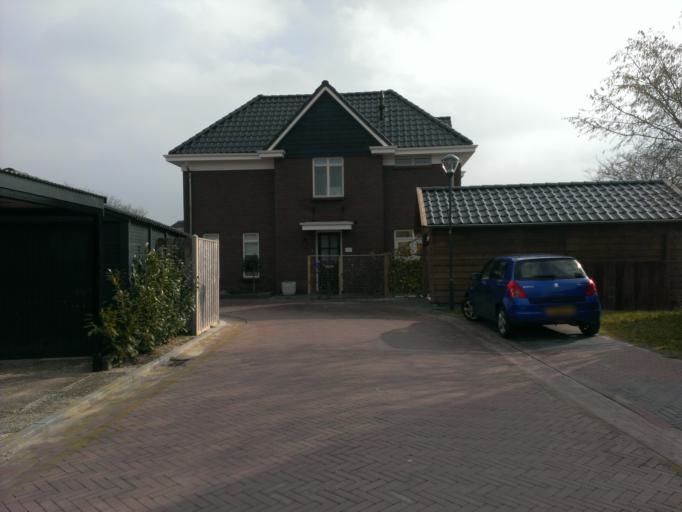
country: NL
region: Gelderland
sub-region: Gemeente Voorst
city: Twello
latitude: 52.2342
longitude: 6.0948
